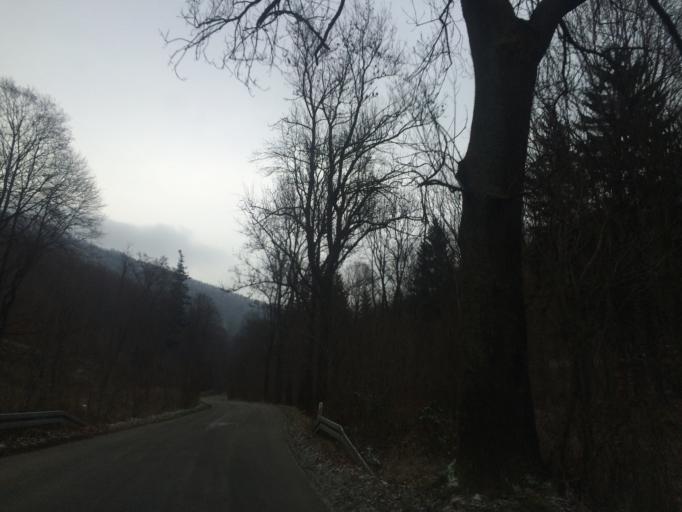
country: PL
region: Lower Silesian Voivodeship
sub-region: Powiat klodzki
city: Stronie Slaskie
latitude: 50.2670
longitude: 16.7623
